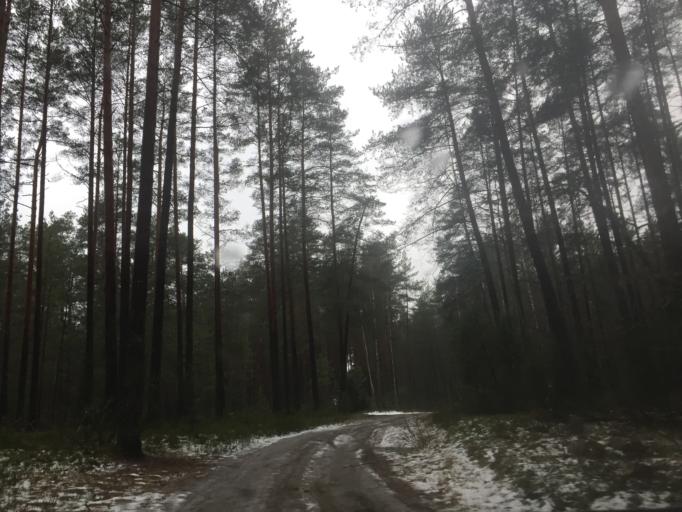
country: LV
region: Stopini
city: Ulbroka
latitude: 56.9500
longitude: 24.3405
